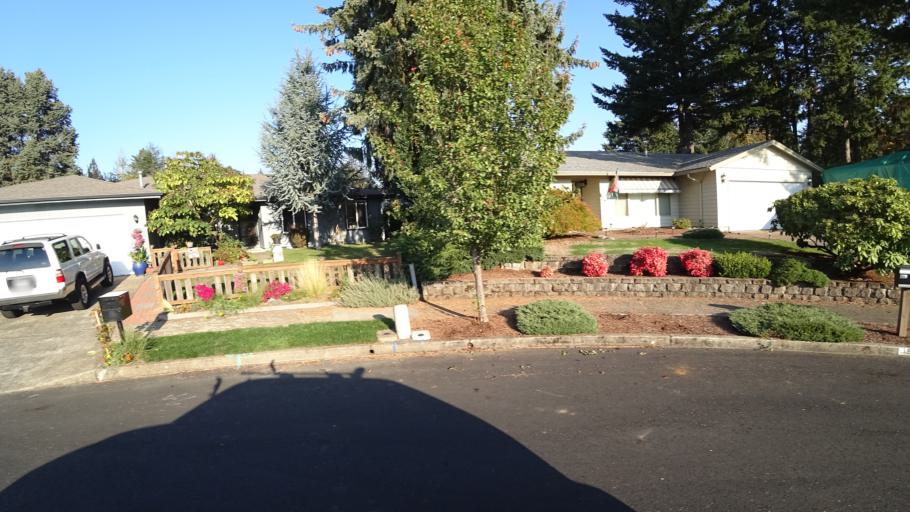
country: US
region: Oregon
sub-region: Multnomah County
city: Gresham
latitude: 45.5078
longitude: -122.4489
